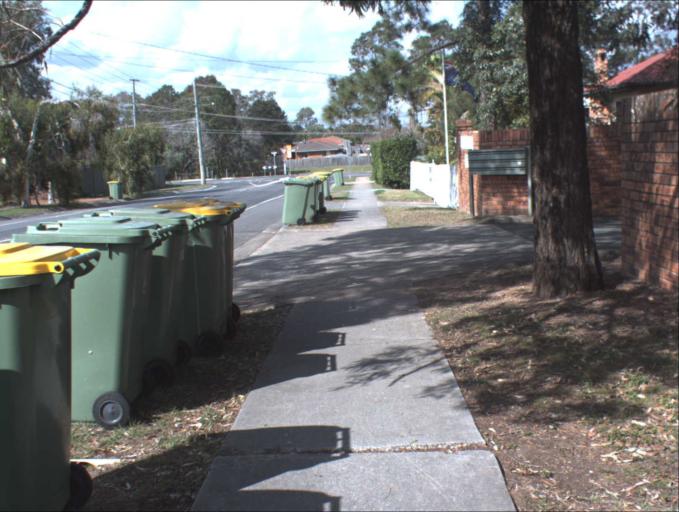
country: AU
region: Queensland
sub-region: Logan
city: Waterford West
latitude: -27.6861
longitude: 153.1328
